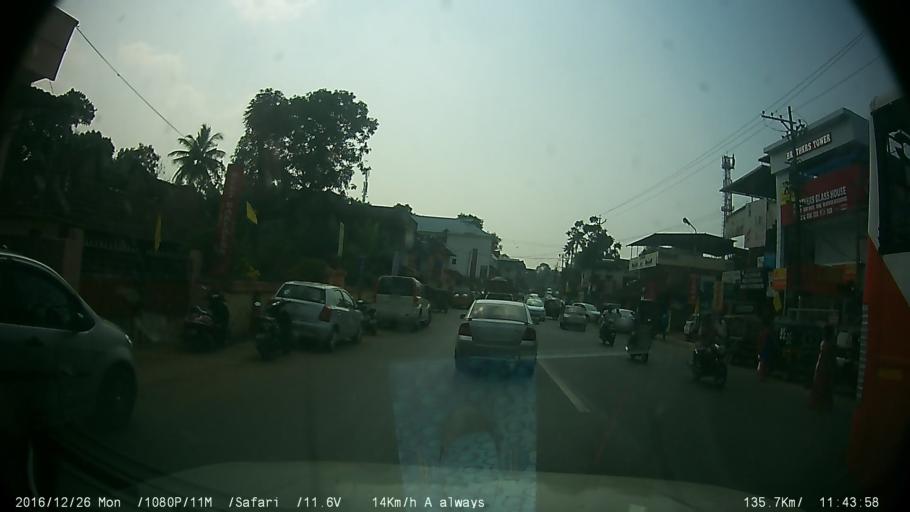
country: IN
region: Kerala
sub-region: Kottayam
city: Kottayam
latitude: 9.5205
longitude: 76.5251
